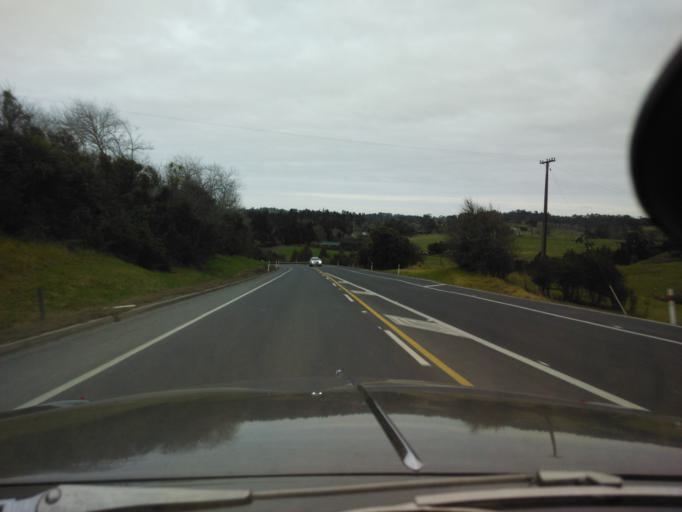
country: NZ
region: Auckland
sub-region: Auckland
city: Rothesay Bay
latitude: -36.6767
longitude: 174.6408
